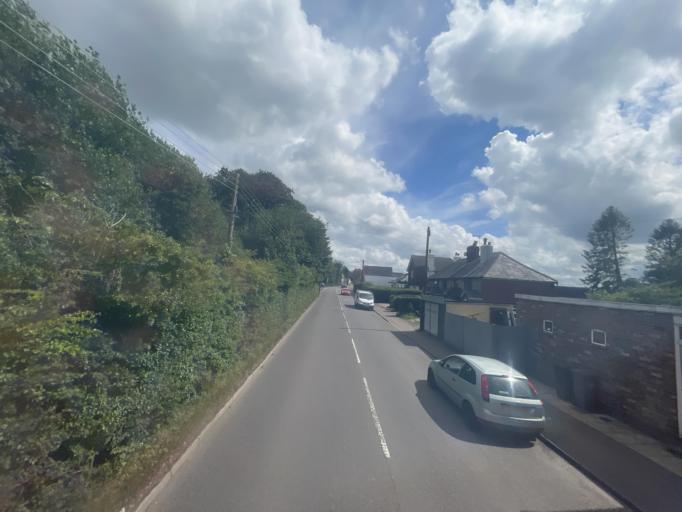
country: GB
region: England
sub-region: Kent
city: Biggin Hill
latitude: 51.3025
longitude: 0.0518
